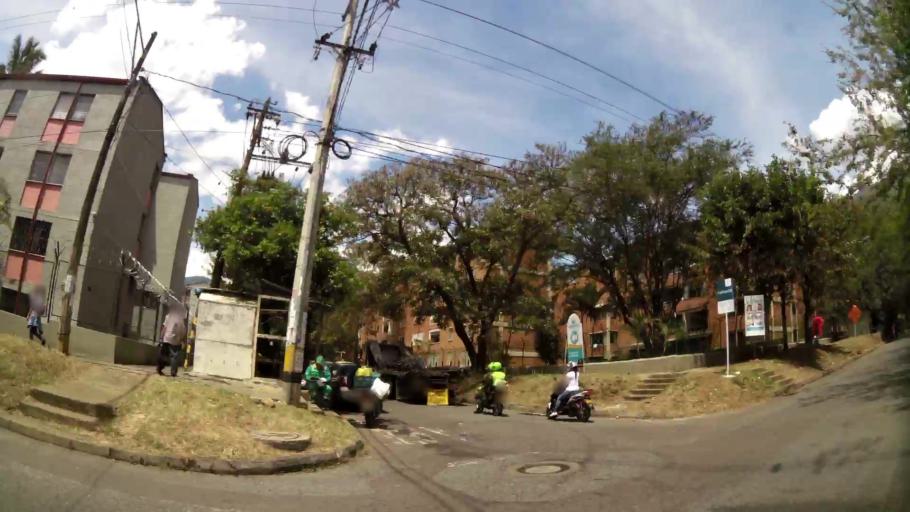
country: CO
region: Antioquia
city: Bello
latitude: 6.3425
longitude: -75.5461
